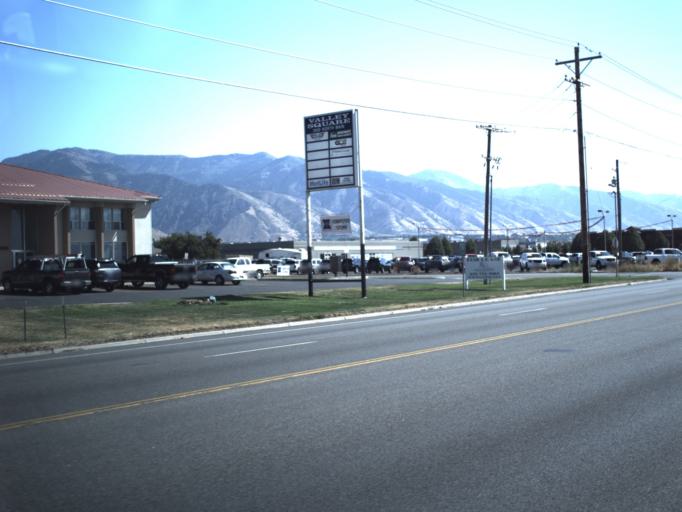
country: US
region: Utah
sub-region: Cache County
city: Hyde Park
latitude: 41.7807
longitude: -111.8340
